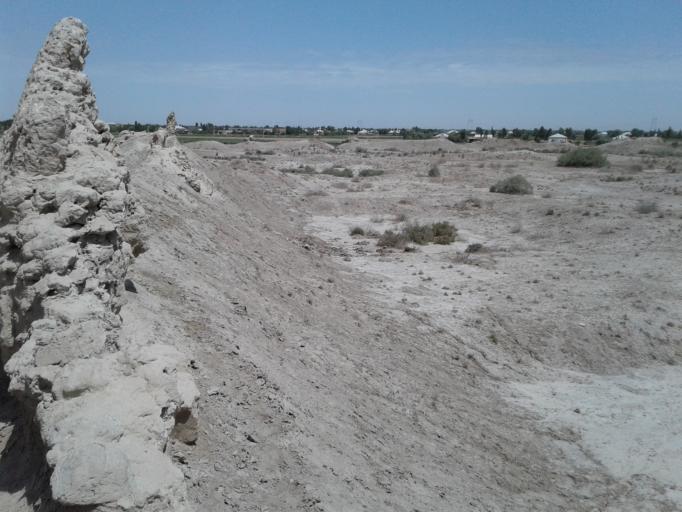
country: TM
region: Dasoguz
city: Tagta
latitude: 41.5411
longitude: 59.9982
